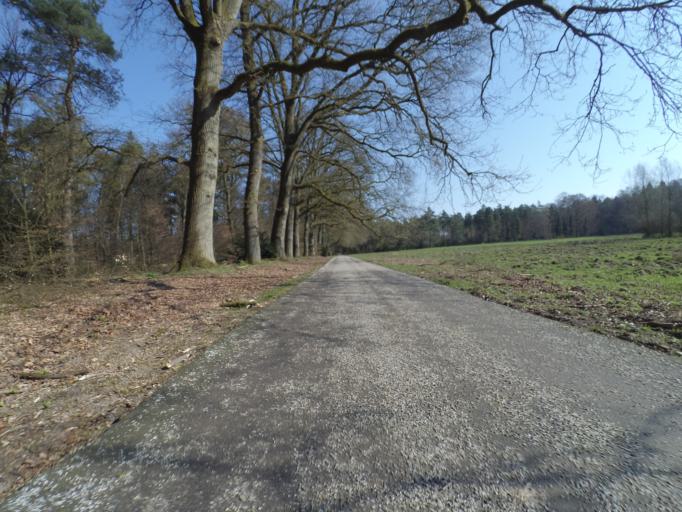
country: NL
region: Gelderland
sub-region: Gemeente Ede
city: Otterlo
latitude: 52.1026
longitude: 5.8387
